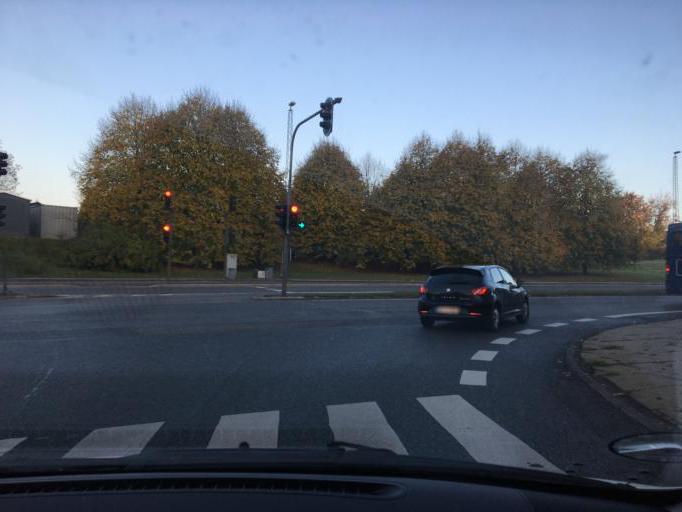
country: DK
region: South Denmark
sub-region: Vejle Kommune
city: Vejle
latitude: 55.6912
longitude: 9.5222
